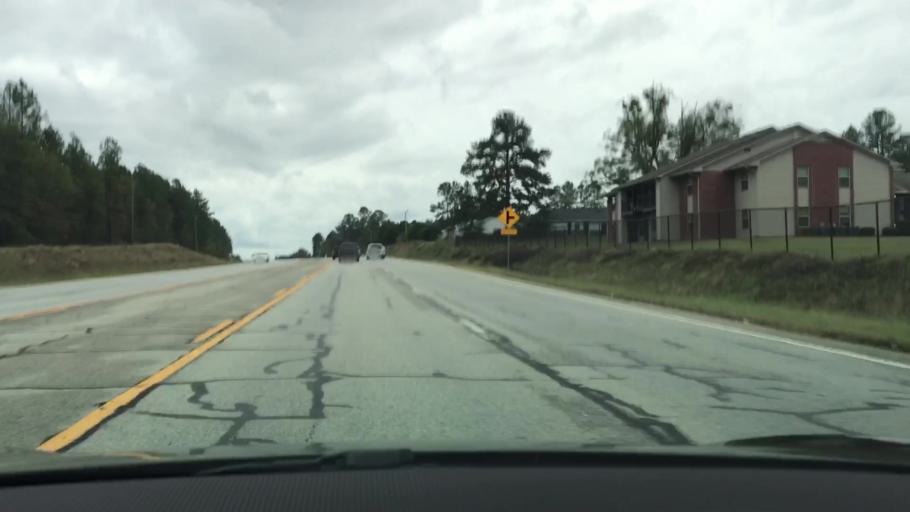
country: US
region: Georgia
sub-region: Jefferson County
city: Wadley
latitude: 32.8759
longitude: -82.3960
